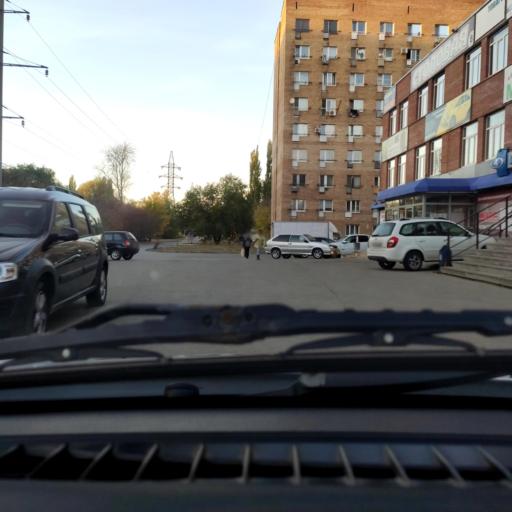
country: RU
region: Samara
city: Tol'yatti
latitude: 53.5106
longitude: 49.4518
